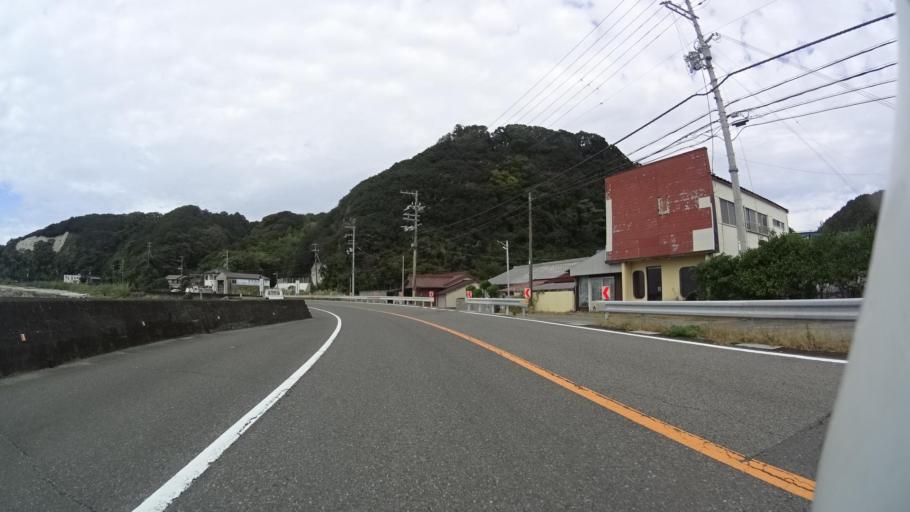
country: JP
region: Wakayama
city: Shingu
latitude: 33.4842
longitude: 135.7600
